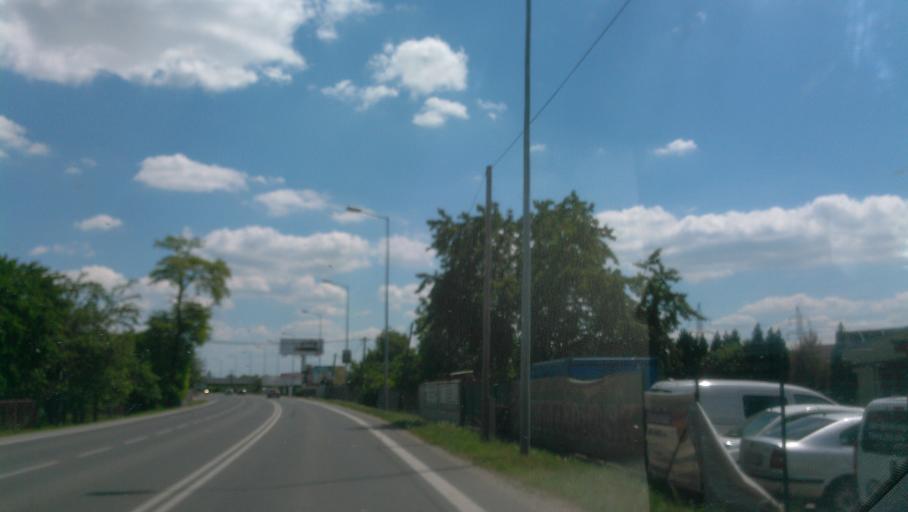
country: SK
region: Bratislavsky
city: Dunajska Luzna
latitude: 48.1249
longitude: 17.1977
